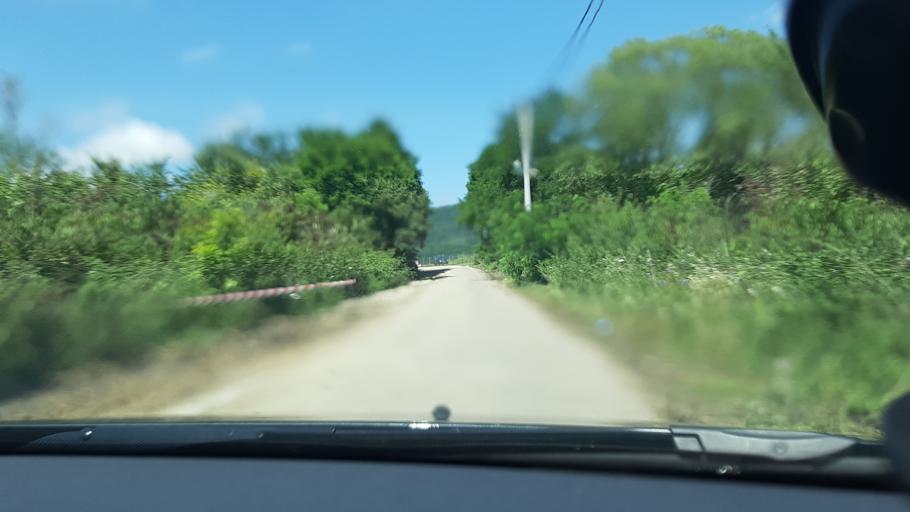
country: RO
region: Hunedoara
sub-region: Comuna Teliucu Inferior
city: Teliucu Inferior
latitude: 45.6891
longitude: 22.8683
